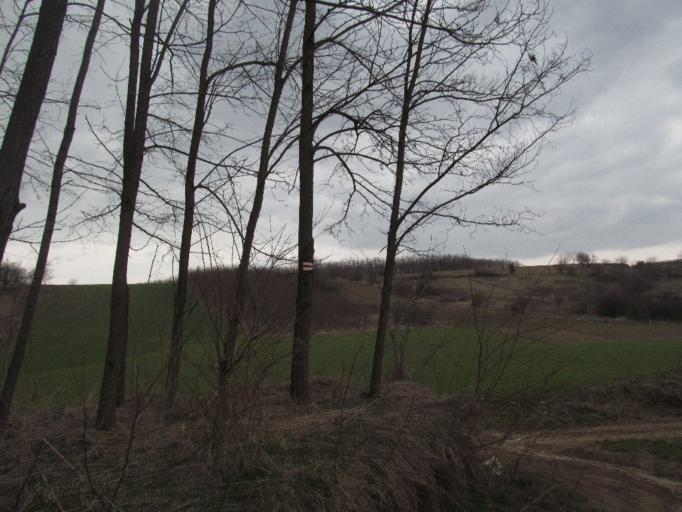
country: HU
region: Gyor-Moson-Sopron
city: Pannonhalma
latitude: 47.5190
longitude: 17.7356
